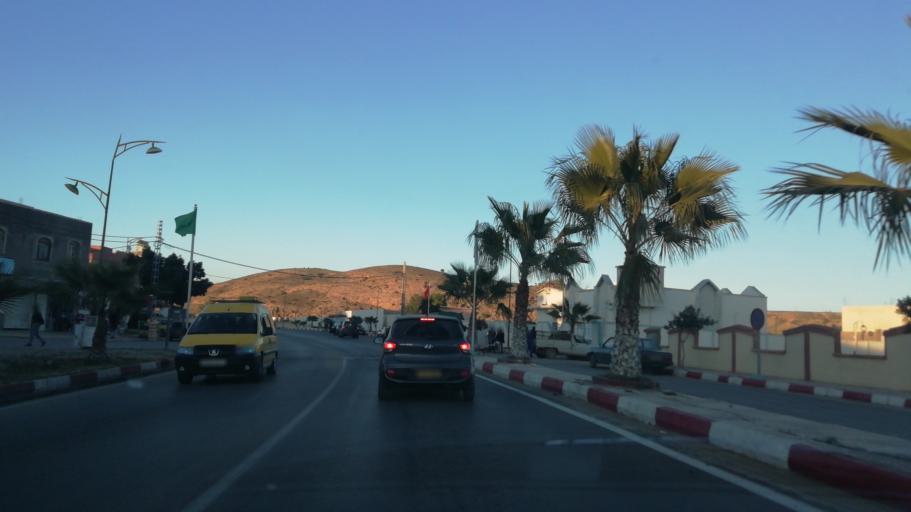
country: DZ
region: Tlemcen
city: Nedroma
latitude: 34.8934
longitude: -1.6365
